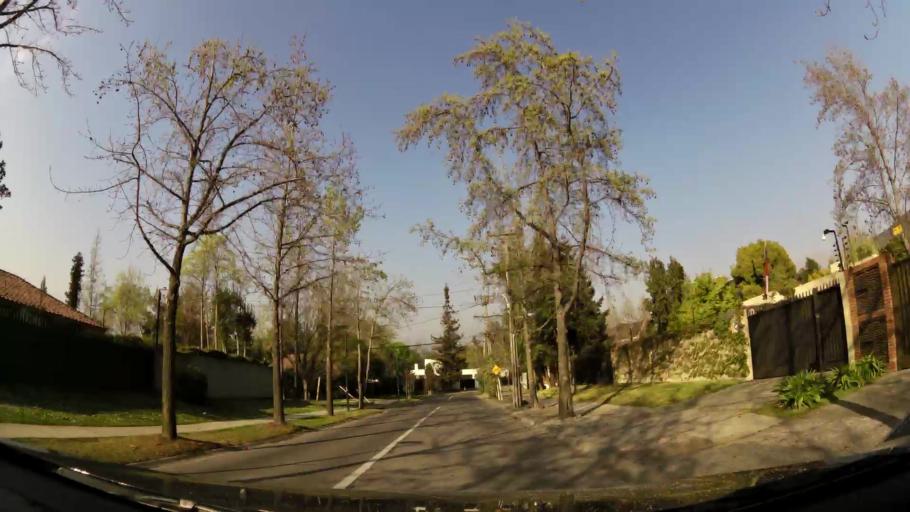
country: CL
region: Santiago Metropolitan
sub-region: Provincia de Santiago
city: Villa Presidente Frei, Nunoa, Santiago, Chile
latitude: -33.3637
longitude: -70.5356
